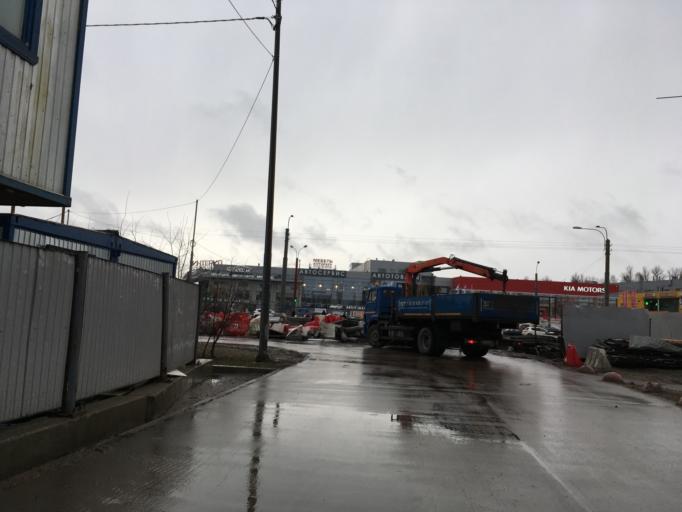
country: RU
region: St.-Petersburg
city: Komendantsky aerodrom
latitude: 60.0001
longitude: 30.2691
